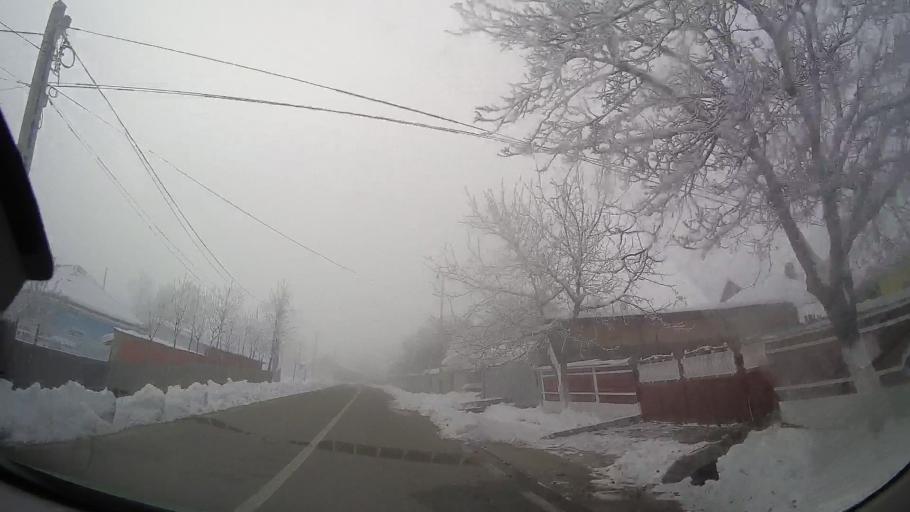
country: RO
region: Iasi
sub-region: Comuna Valea Seaca
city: Topile
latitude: 47.2665
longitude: 26.6706
